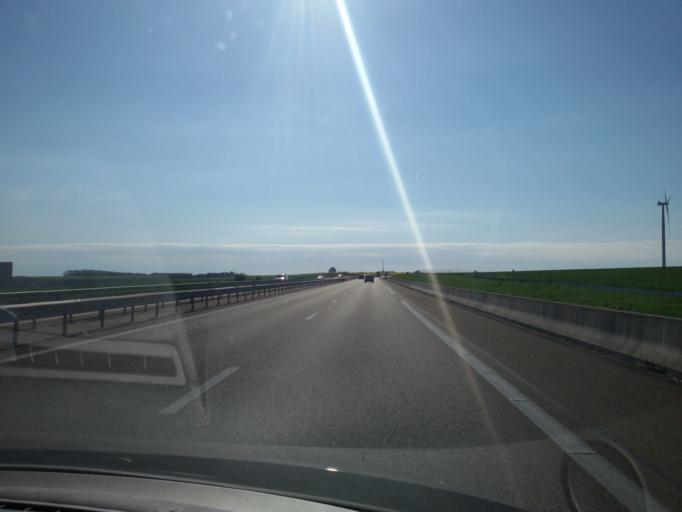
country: FR
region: Bourgogne
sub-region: Departement de l'Yonne
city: Saint-Bris-le-Vineux
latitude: 47.7743
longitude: 3.7129
